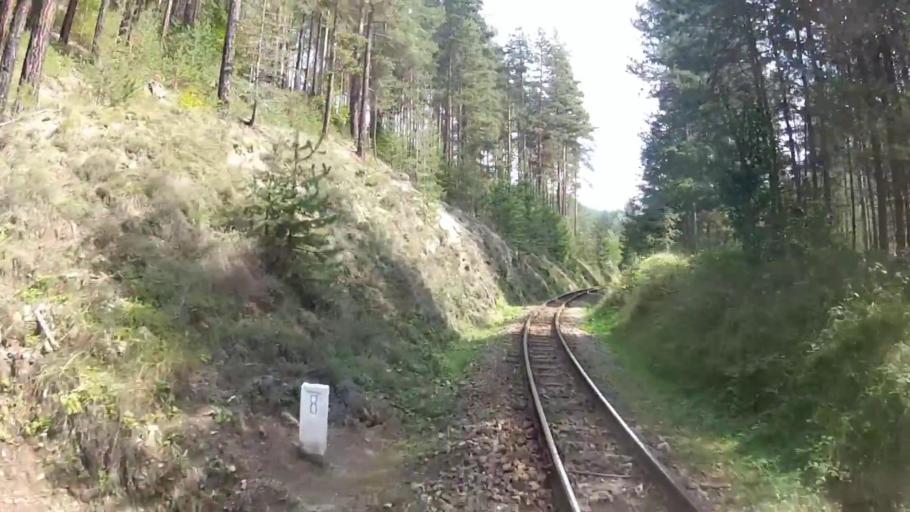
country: BG
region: Blagoevgrad
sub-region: Obshtina Yakoruda
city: Yakoruda
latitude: 42.0323
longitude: 23.7573
